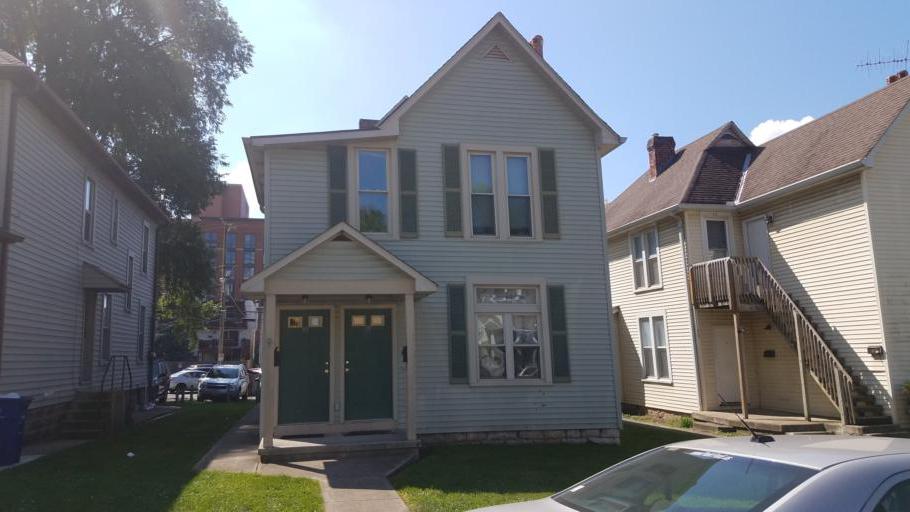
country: US
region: Ohio
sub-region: Franklin County
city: Grandview Heights
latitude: 40.0073
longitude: -83.0120
